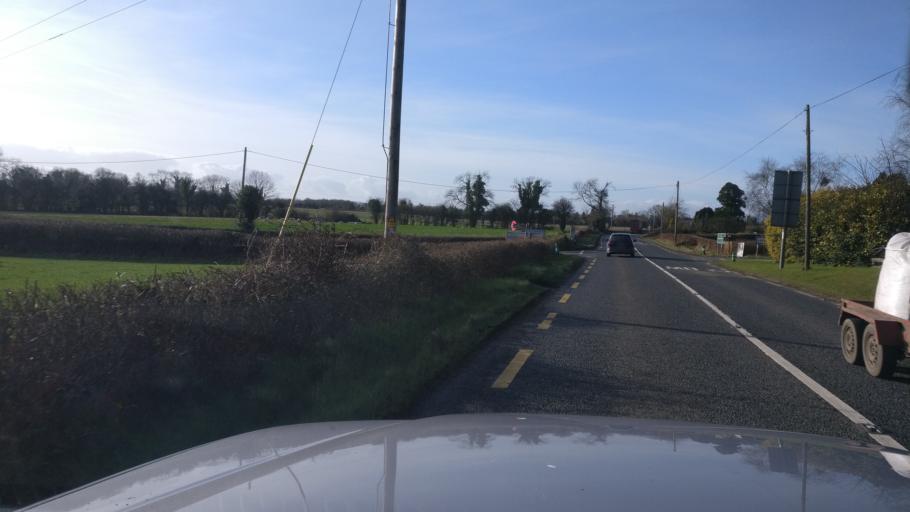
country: IE
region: Leinster
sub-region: Uibh Fhaili
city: Tullamore
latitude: 53.1978
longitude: -7.4204
